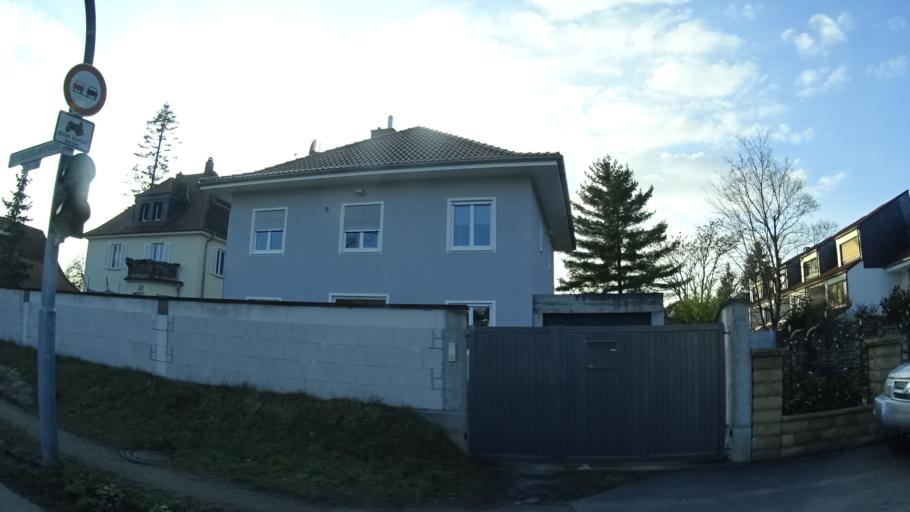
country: DE
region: Hesse
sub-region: Regierungsbezirk Darmstadt
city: Darmstadt
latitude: 49.8293
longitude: 8.6448
